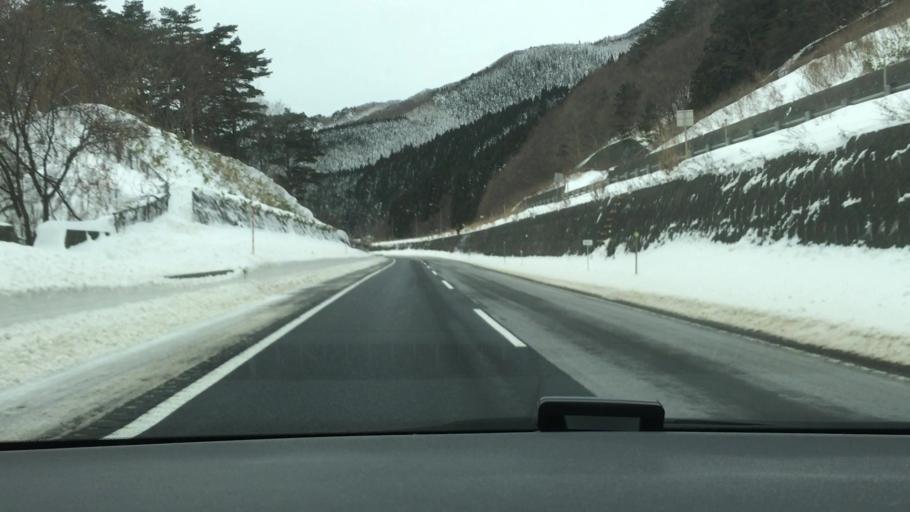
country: JP
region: Akita
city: Hanawa
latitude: 40.1228
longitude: 140.8417
